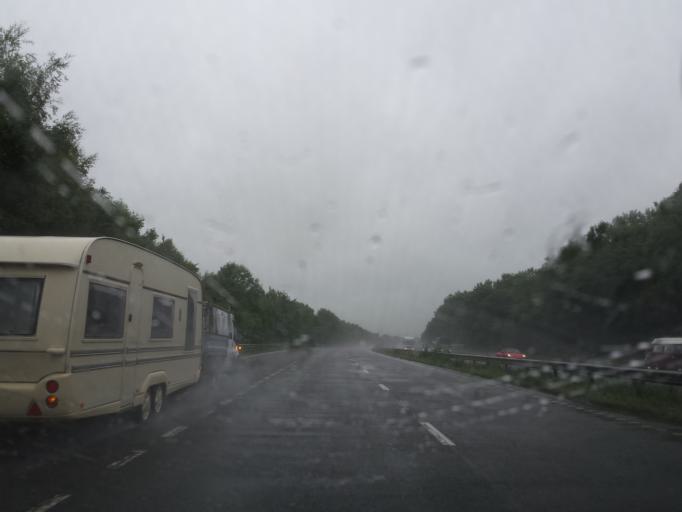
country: GB
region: England
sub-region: Warwickshire
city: Kenilworth
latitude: 52.3182
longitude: -1.5697
